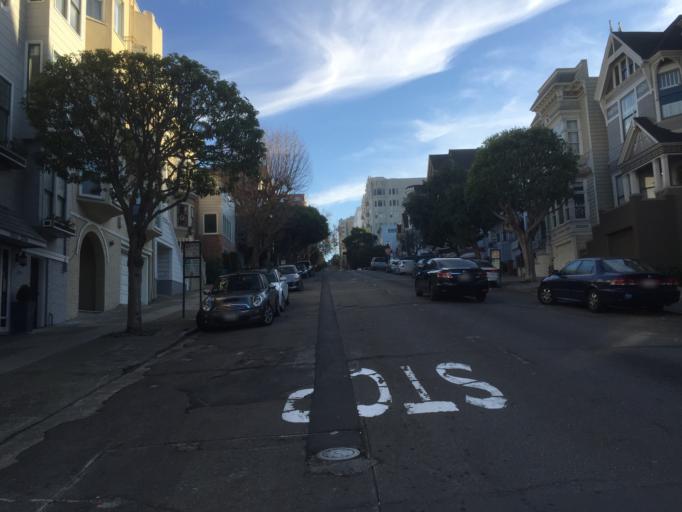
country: US
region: California
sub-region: San Francisco County
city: San Francisco
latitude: 37.7972
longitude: -122.4271
